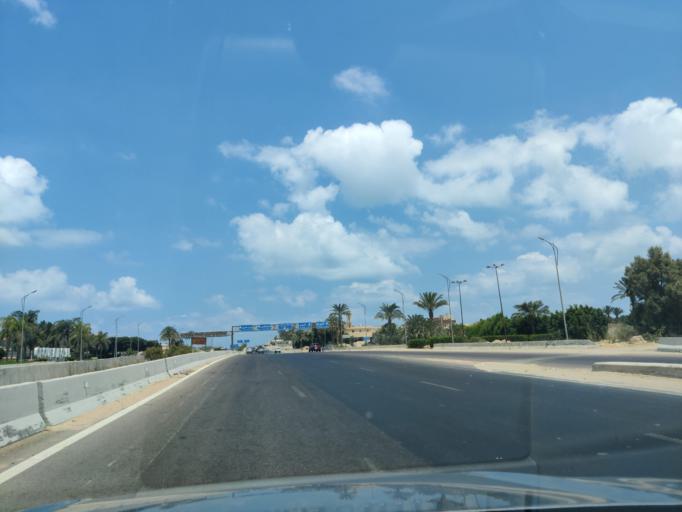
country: EG
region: Alexandria
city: Alexandria
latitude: 31.0072
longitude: 29.6388
